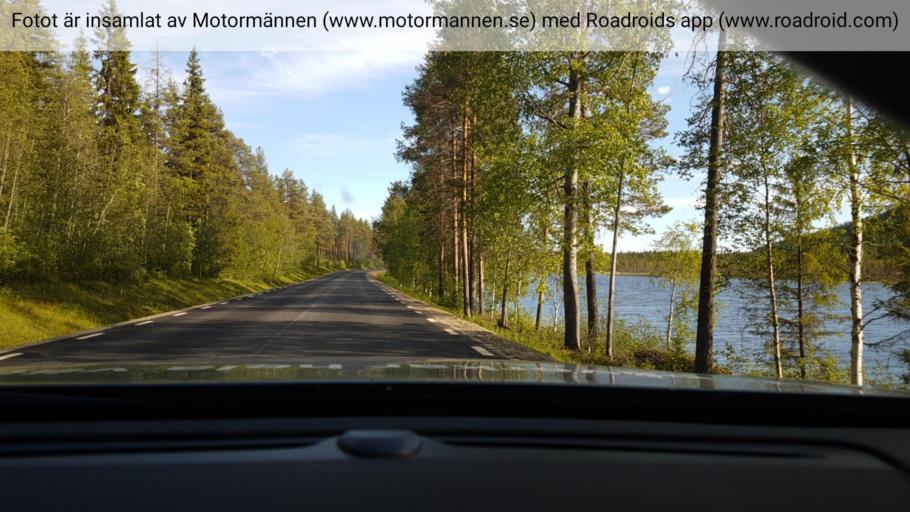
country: SE
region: Vaesterbotten
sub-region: Vindelns Kommun
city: Vindeln
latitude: 64.4399
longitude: 19.3437
